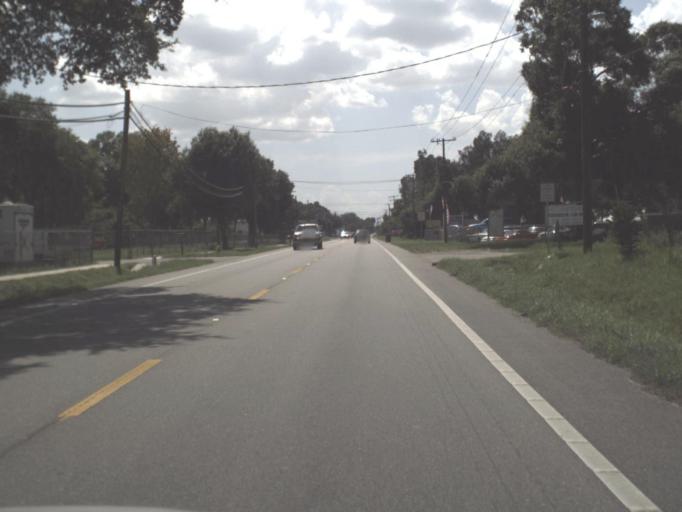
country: US
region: Florida
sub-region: Hillsborough County
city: Mango
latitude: 27.9967
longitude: -82.3290
